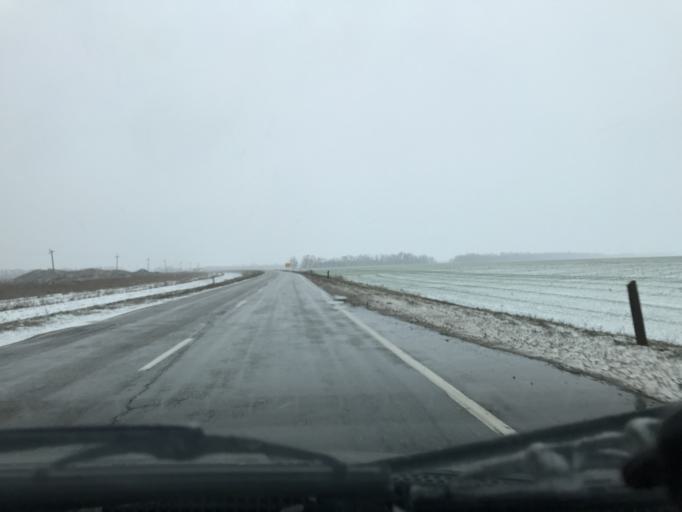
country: RU
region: Rostov
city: Yegorlykskaya
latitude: 46.5477
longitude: 40.6540
